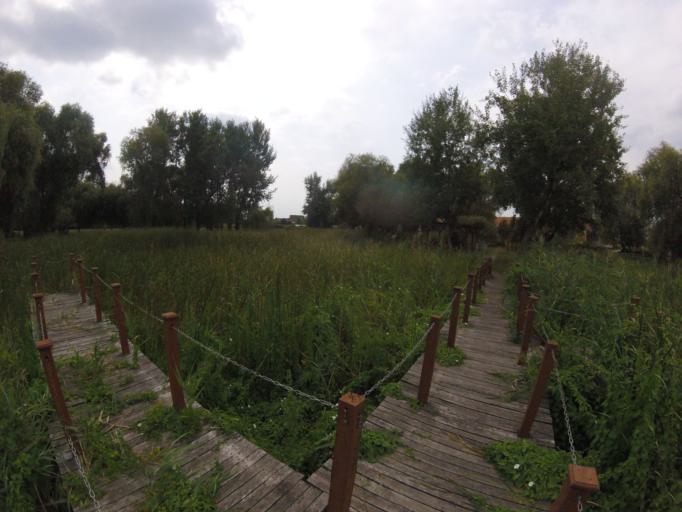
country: HU
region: Szabolcs-Szatmar-Bereg
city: Levelek
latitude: 48.0163
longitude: 21.9629
